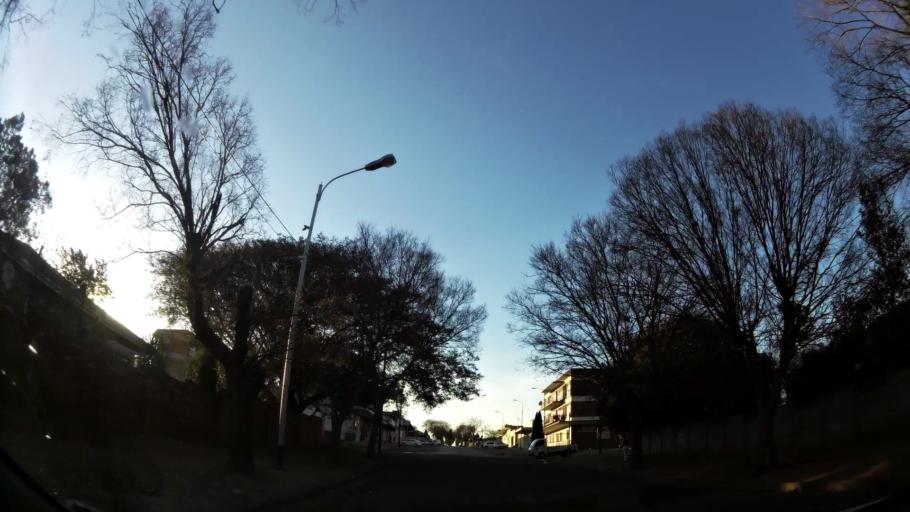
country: ZA
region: Gauteng
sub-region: City of Johannesburg Metropolitan Municipality
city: Roodepoort
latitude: -26.1746
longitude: 27.9300
